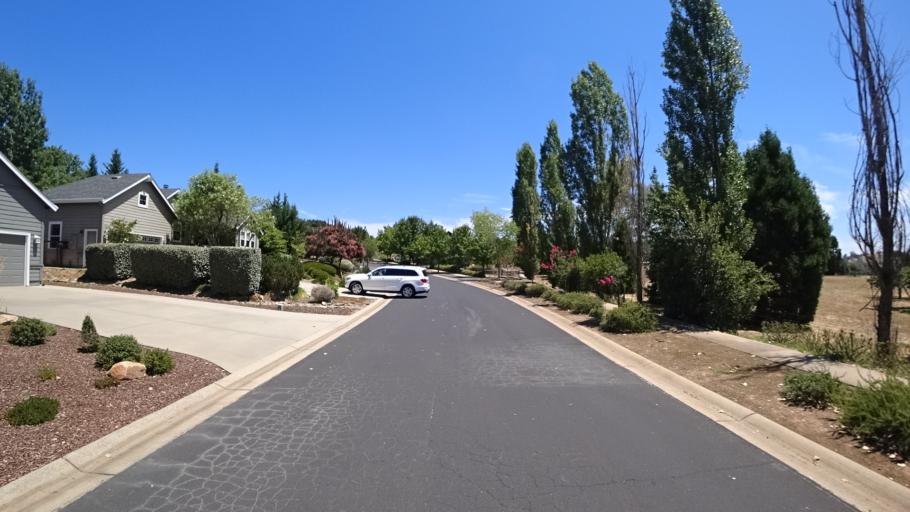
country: US
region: California
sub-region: Calaveras County
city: Angels Camp
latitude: 38.0620
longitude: -120.5520
